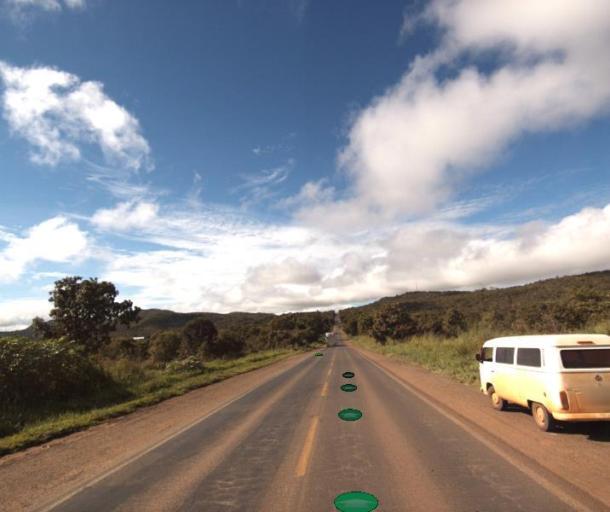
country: BR
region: Goias
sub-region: Uruacu
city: Uruacu
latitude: -14.5485
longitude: -49.1603
